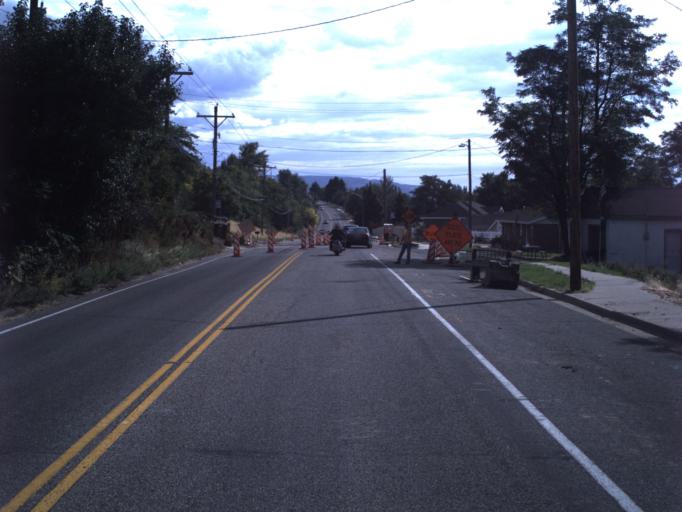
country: US
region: Utah
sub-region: Davis County
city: Farmington
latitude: 40.9569
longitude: -111.8834
